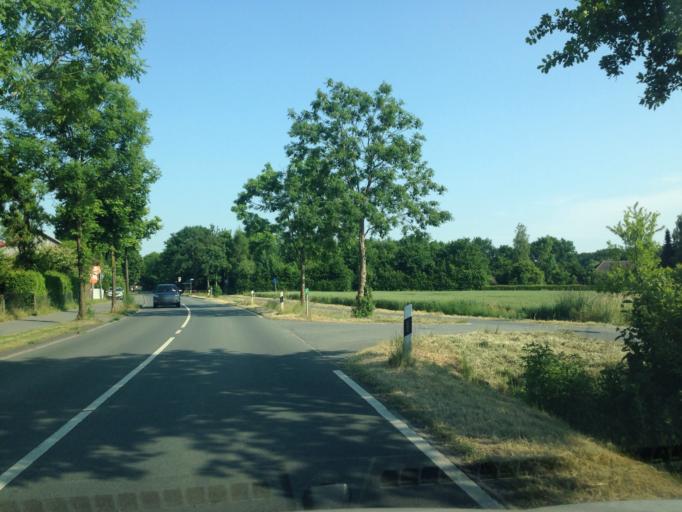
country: DE
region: North Rhine-Westphalia
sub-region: Regierungsbezirk Munster
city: Muenster
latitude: 51.9787
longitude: 7.5551
